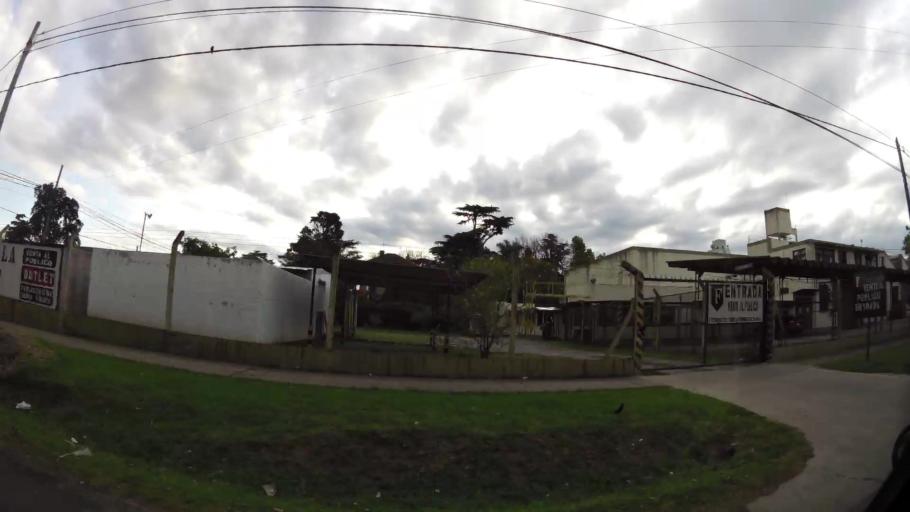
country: AR
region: Buenos Aires
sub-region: Partido de Quilmes
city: Quilmes
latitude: -34.7266
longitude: -58.2395
